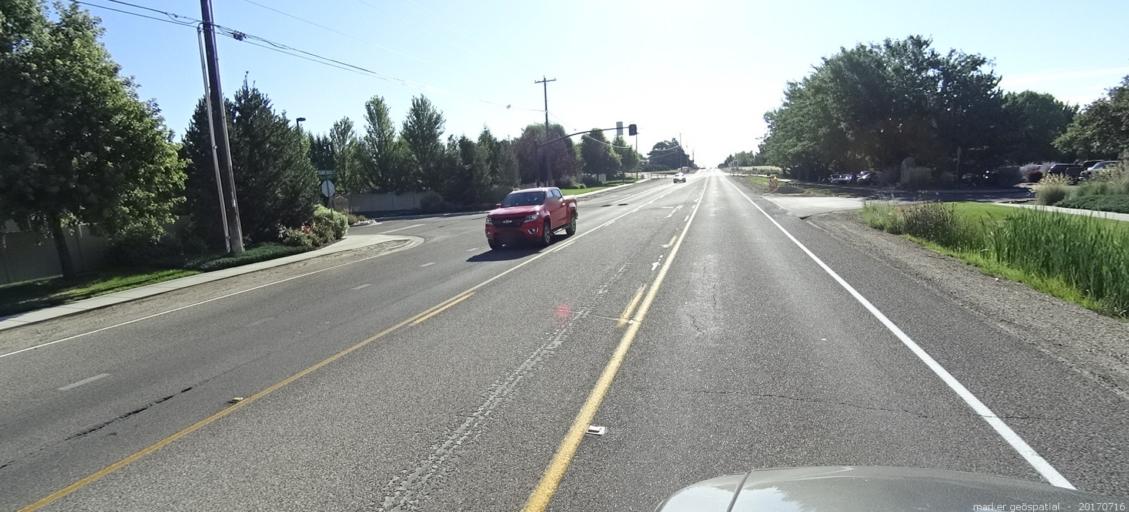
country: US
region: Idaho
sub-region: Ada County
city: Meridian
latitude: 43.5466
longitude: -116.3263
